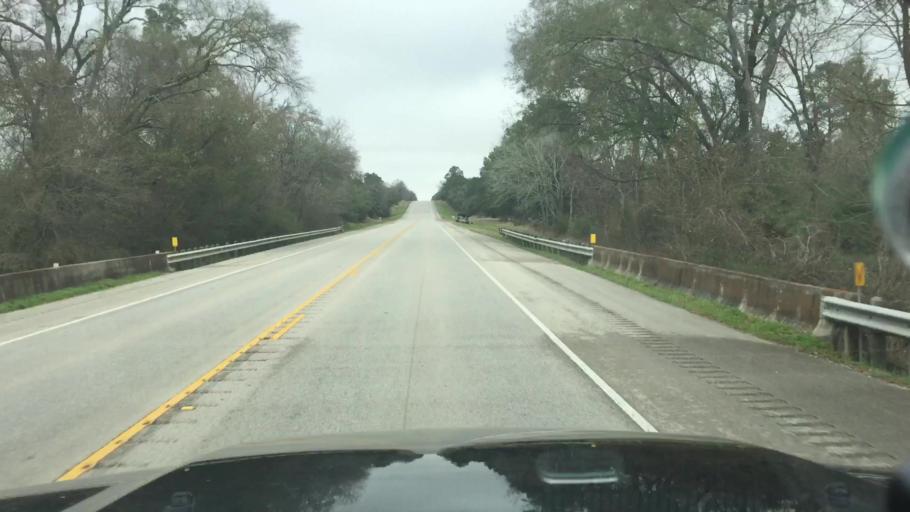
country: US
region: Texas
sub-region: Lee County
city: Giddings
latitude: 30.0681
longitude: -96.9166
